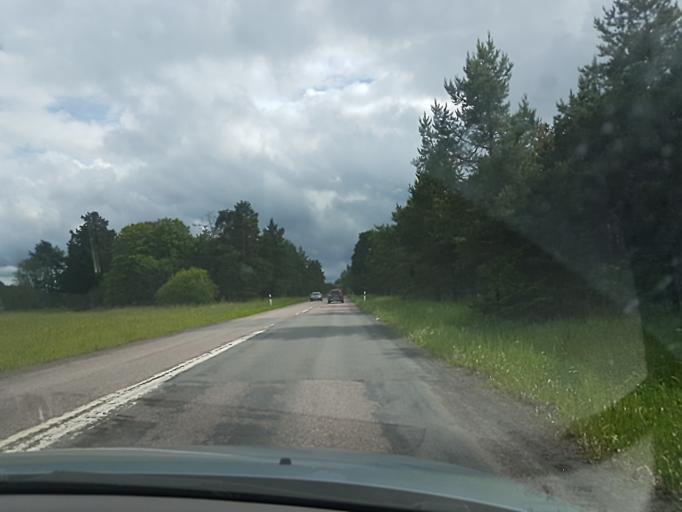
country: SE
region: Uppsala
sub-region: Osthammars Kommun
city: OEsthammar
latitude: 60.2483
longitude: 18.3476
